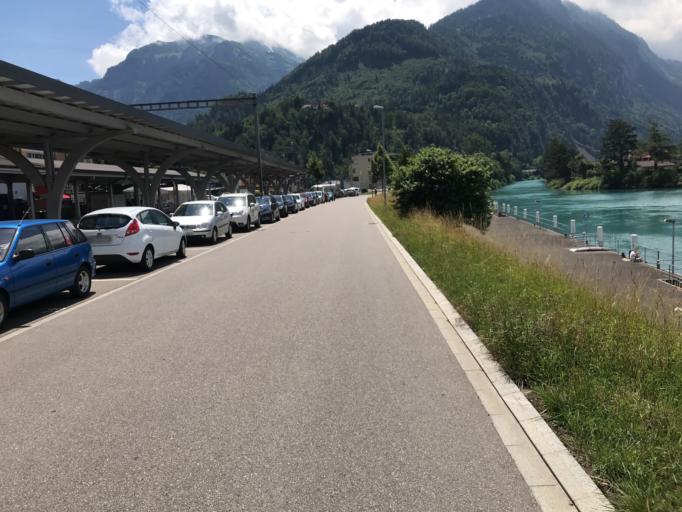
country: CH
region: Bern
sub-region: Interlaken-Oberhasli District
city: Unterseen
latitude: 46.6825
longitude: 7.8511
